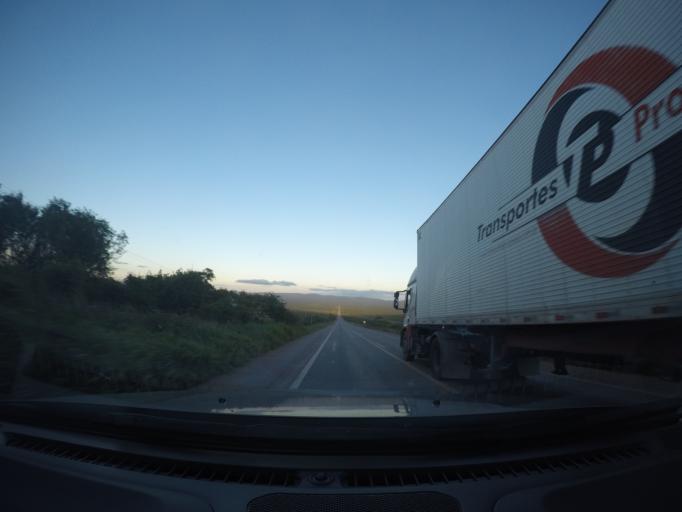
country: BR
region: Bahia
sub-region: Seabra
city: Seabra
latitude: -12.4127
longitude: -41.9755
